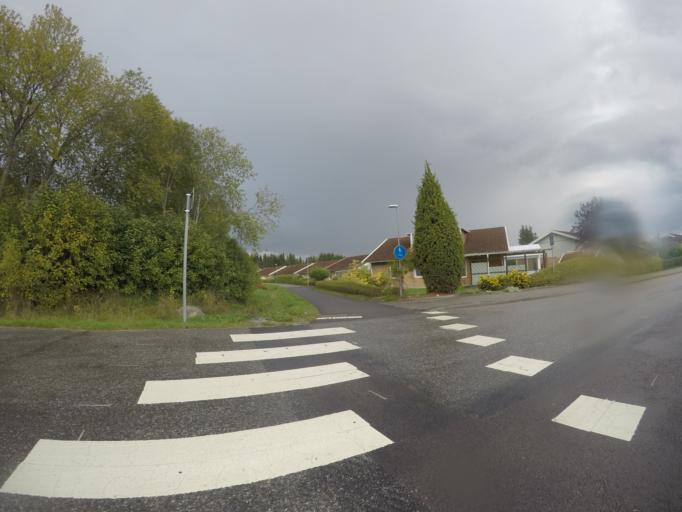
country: SE
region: Vaestmanland
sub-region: Vasteras
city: Vasteras
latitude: 59.6511
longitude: 16.5288
